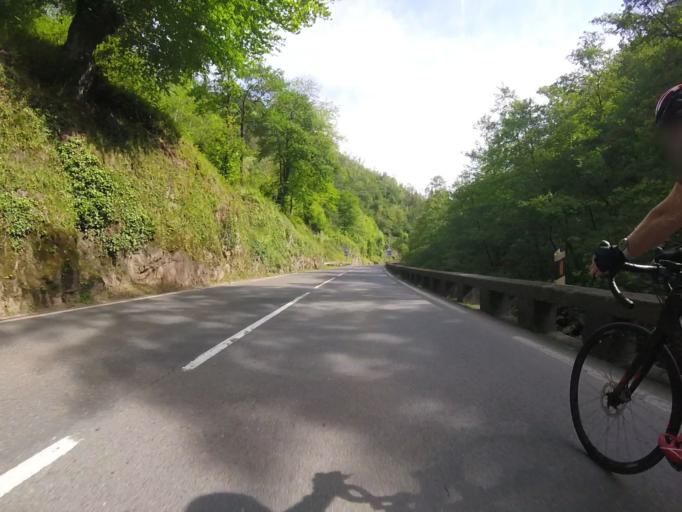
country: ES
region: Basque Country
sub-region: Provincia de Guipuzcoa
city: Anzuola
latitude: 43.1383
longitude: -2.3511
